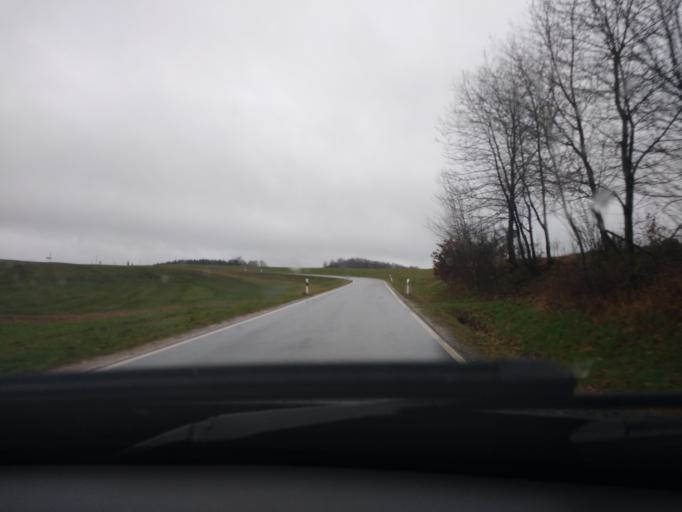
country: DE
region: Rheinland-Pfalz
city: Paschel
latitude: 49.6295
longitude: 6.6853
